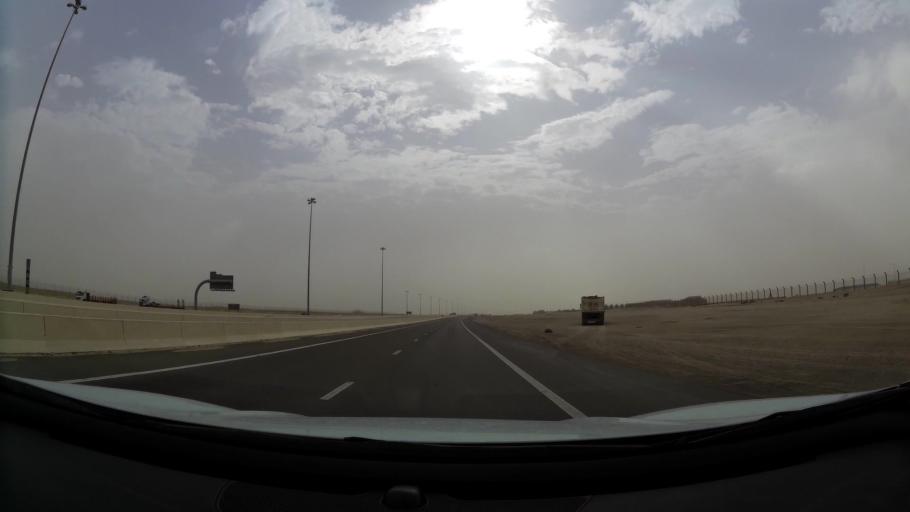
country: AE
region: Abu Dhabi
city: Abu Dhabi
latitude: 24.4794
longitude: 54.6614
